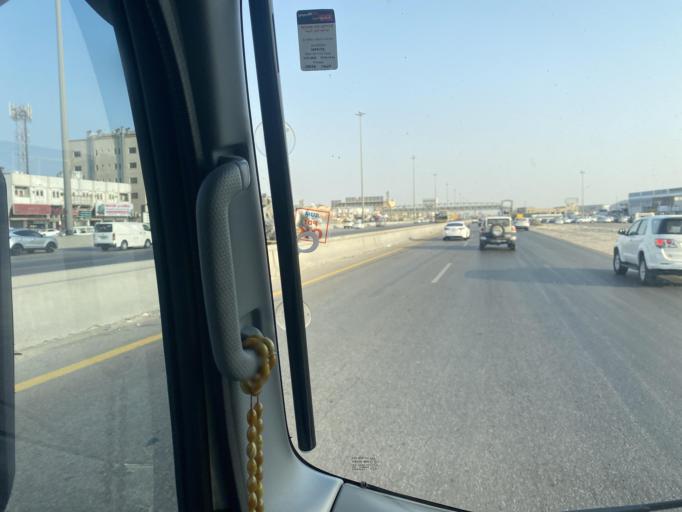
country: SA
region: Eastern Province
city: Sayhat
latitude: 26.4066
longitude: 50.0146
